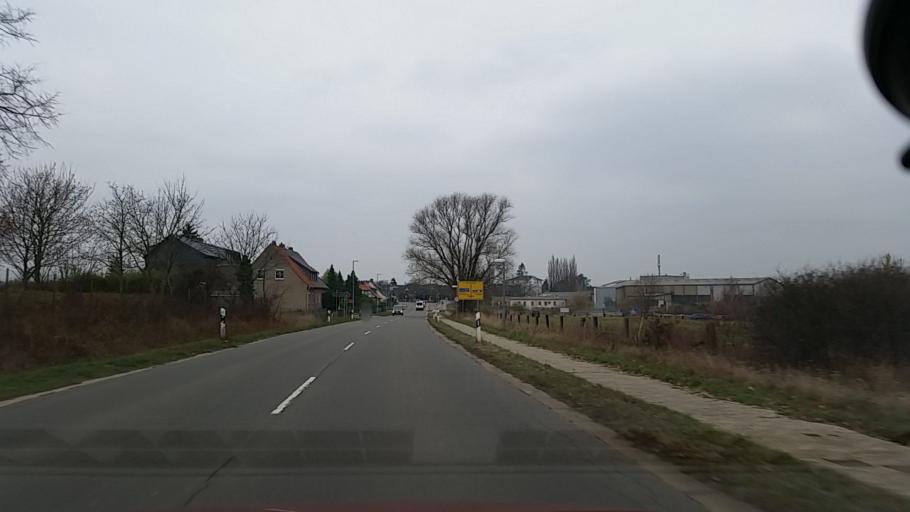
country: DE
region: Lower Saxony
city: Danndorf
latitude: 52.4172
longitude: 10.8518
